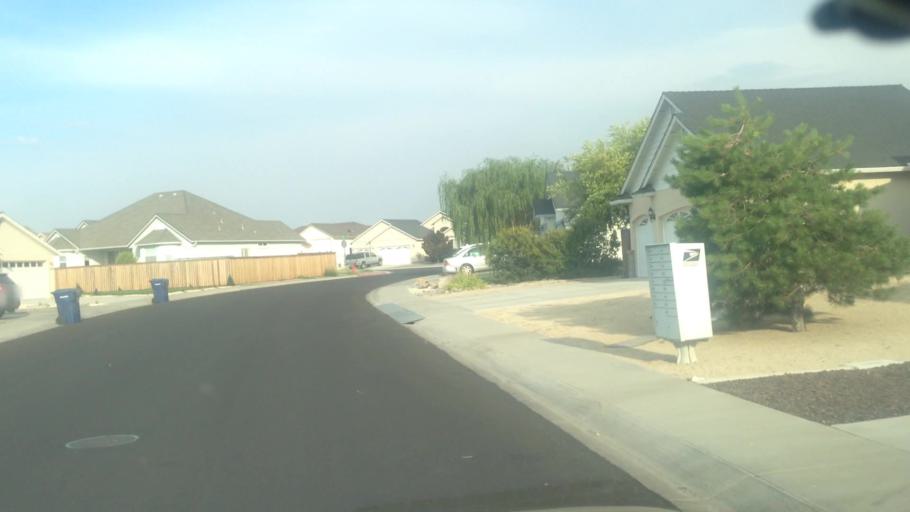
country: US
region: Nevada
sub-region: Lyon County
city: Fernley
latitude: 39.5888
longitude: -119.1531
